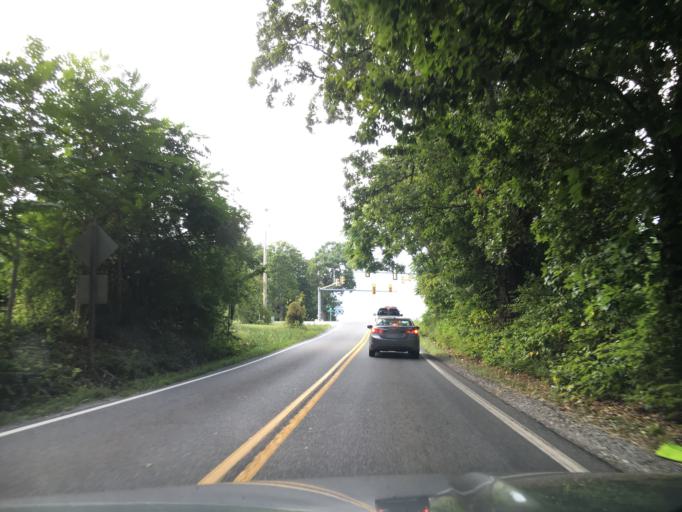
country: US
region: Virginia
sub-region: Campbell County
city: Rustburg
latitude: 37.2615
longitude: -79.1458
